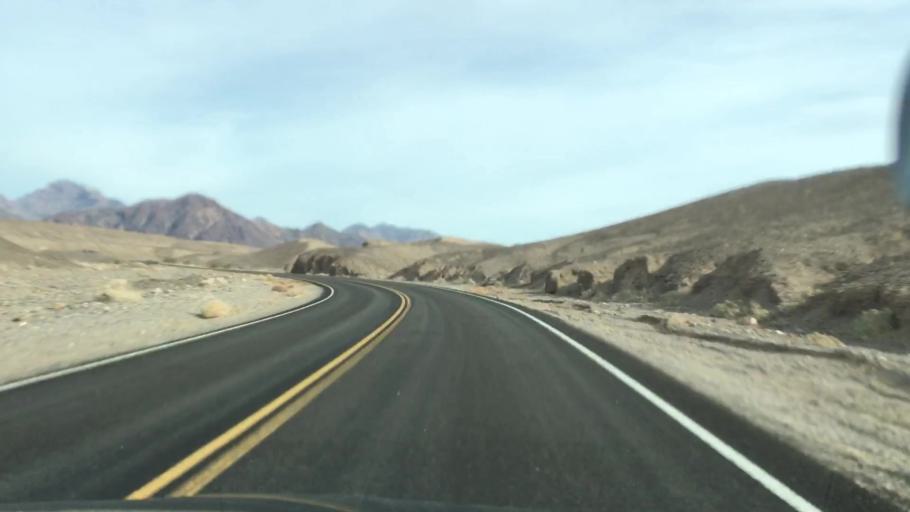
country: US
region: Nevada
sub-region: Nye County
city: Beatty
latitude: 36.6575
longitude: -117.0213
